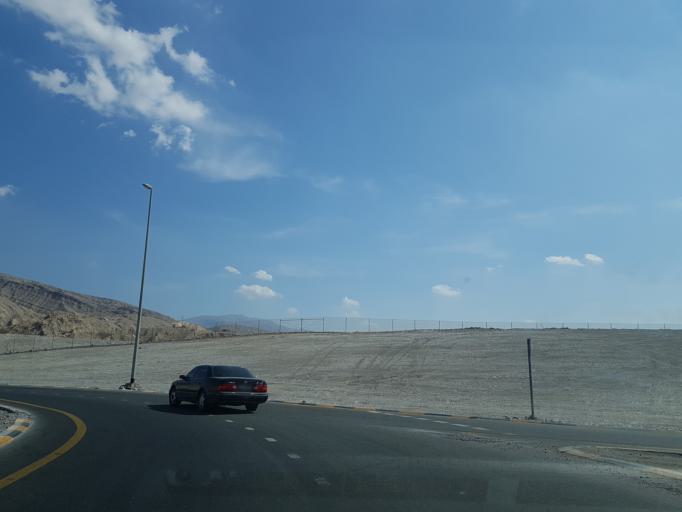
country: AE
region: Ra's al Khaymah
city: Ras al-Khaimah
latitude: 25.7626
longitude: 56.0230
